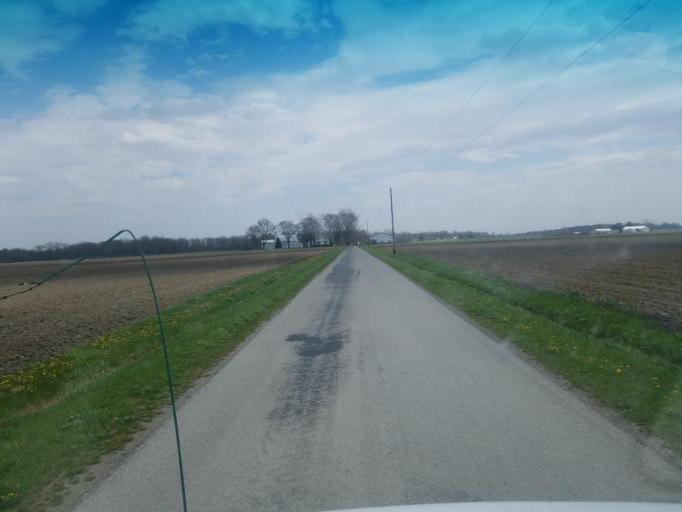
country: US
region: Ohio
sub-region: Wyandot County
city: Upper Sandusky
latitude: 40.7742
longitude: -83.3270
